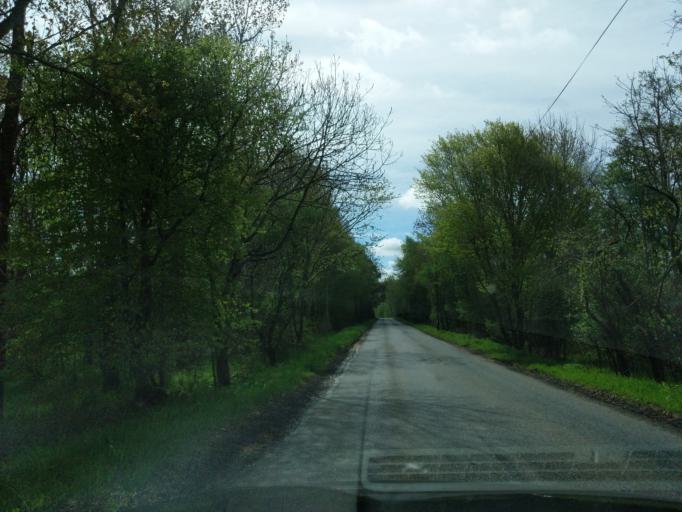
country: GB
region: Scotland
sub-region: The Scottish Borders
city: Saint Boswells
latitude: 55.6338
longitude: -2.5839
